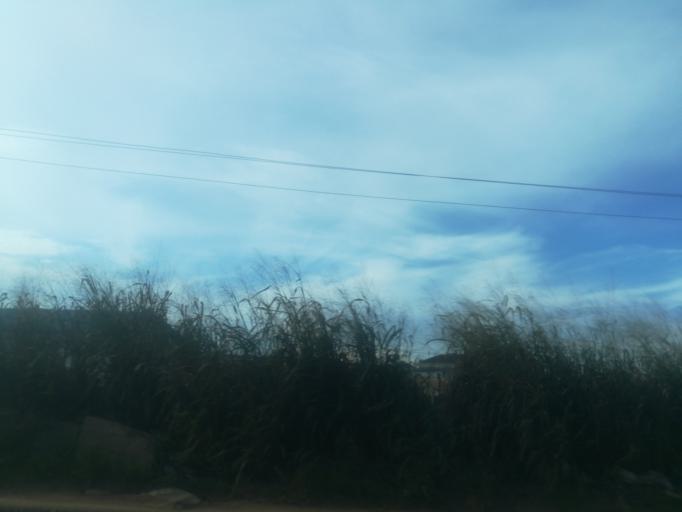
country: NG
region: Oyo
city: Ibadan
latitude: 7.3360
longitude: 3.8909
